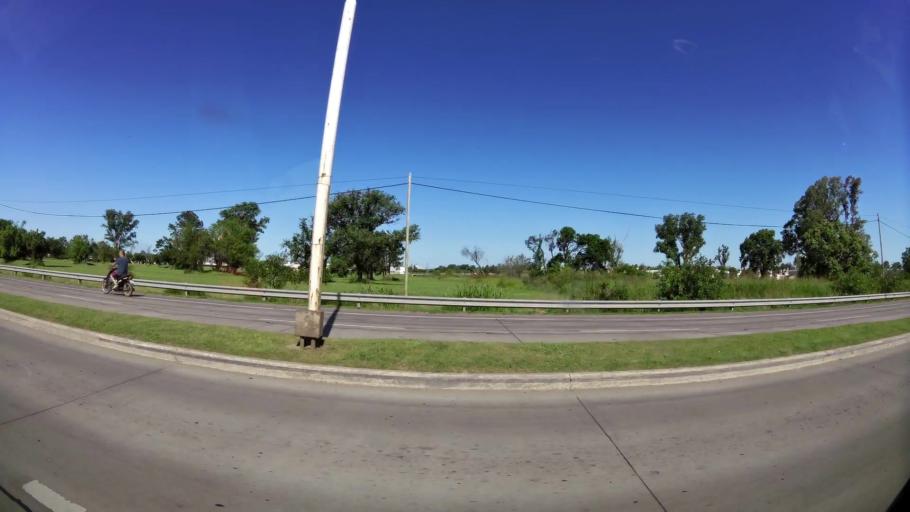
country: AR
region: Santa Fe
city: Rafaela
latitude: -31.2641
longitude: -61.5080
